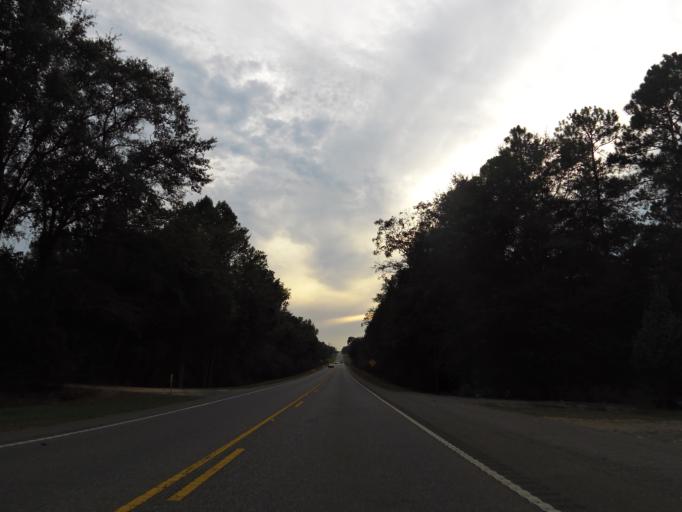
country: US
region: Alabama
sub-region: Escambia County
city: Atmore
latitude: 31.0011
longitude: -87.5961
